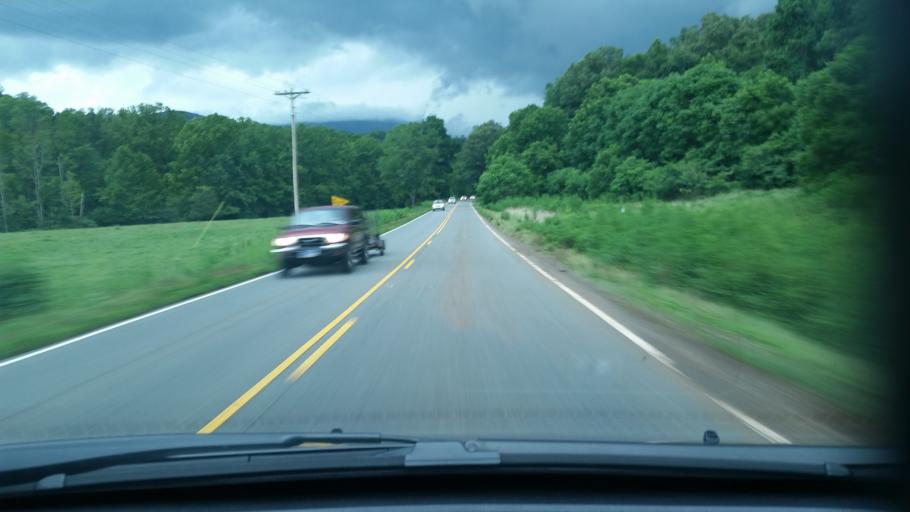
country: US
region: Virginia
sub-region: Nelson County
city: Nellysford
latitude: 37.8925
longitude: -78.8276
